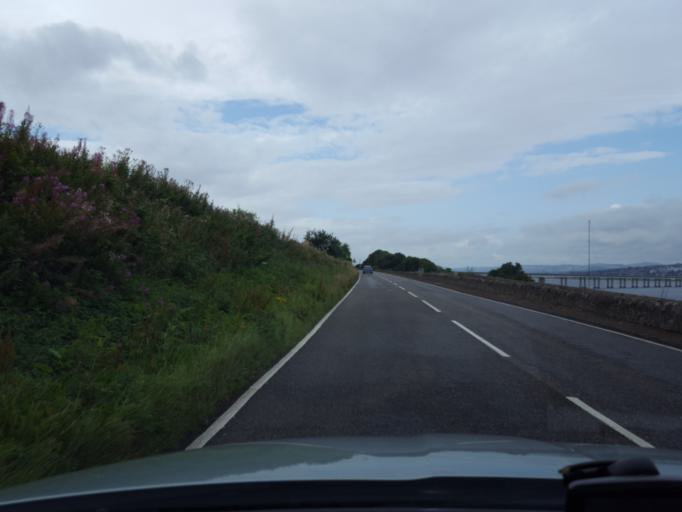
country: GB
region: Scotland
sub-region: Fife
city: Newport-On-Tay
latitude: 56.4496
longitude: -2.9182
